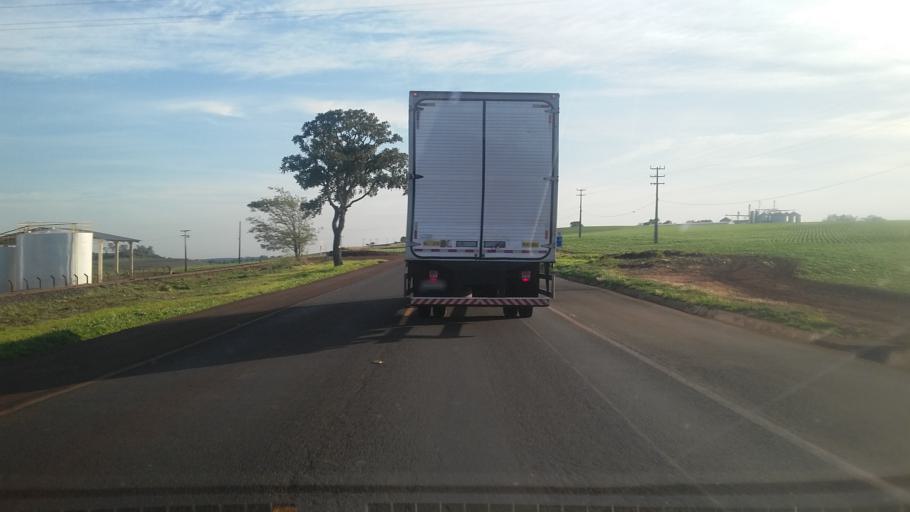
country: BR
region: Parana
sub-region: Bandeirantes
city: Bandeirantes
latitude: -23.1487
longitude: -50.5955
